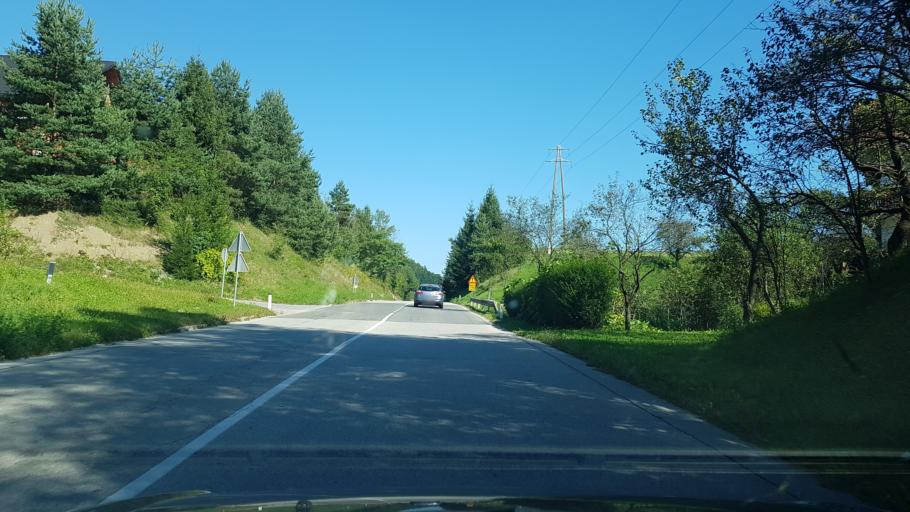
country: SI
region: Sostanj
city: Sostanj
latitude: 46.3627
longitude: 15.0598
